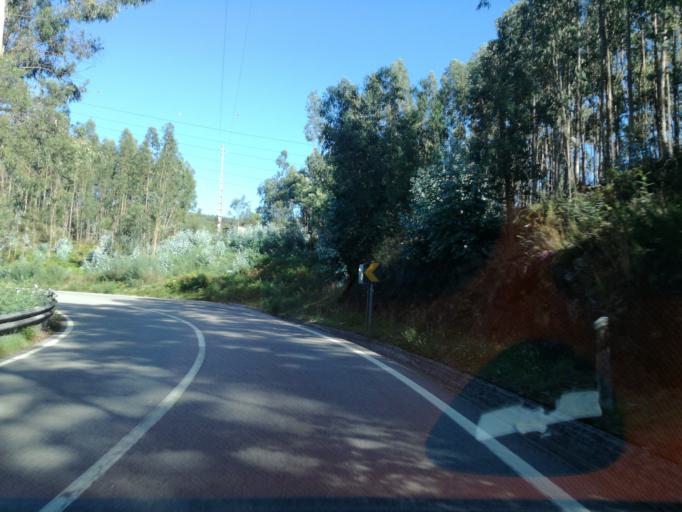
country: PT
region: Porto
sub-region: Pacos de Ferreira
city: Seroa
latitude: 41.2560
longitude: -8.4618
